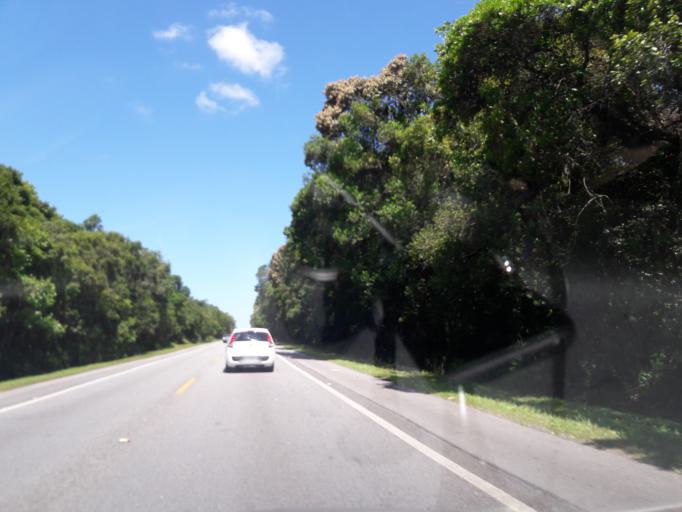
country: BR
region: Parana
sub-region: Pontal Do Parana
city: Pontal do Parana
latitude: -25.6057
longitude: -48.5548
